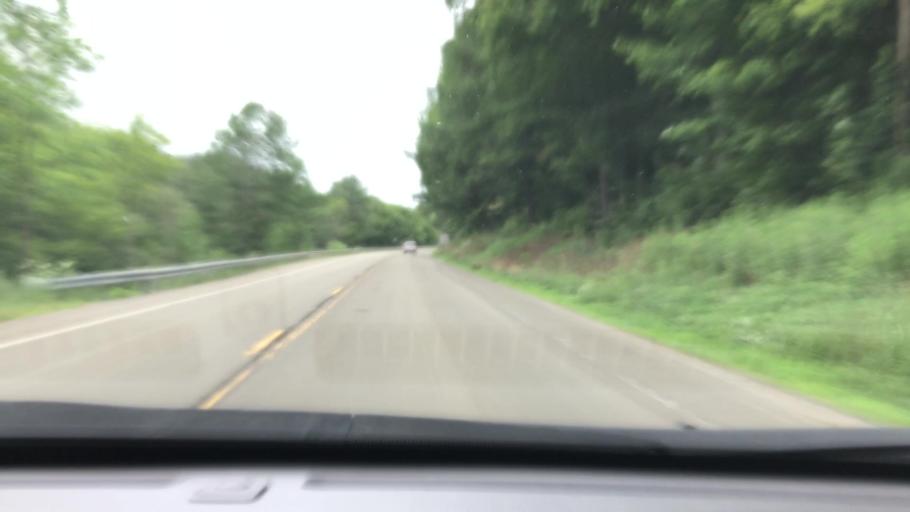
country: US
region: Pennsylvania
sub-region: McKean County
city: Kane
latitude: 41.6593
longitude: -78.6810
